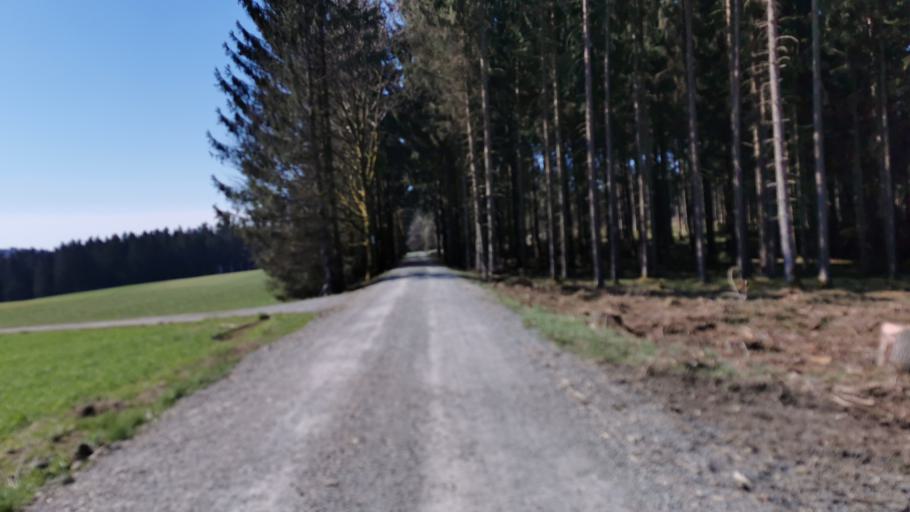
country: DE
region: Bavaria
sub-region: Upper Franconia
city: Pressig
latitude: 50.3895
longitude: 11.3344
